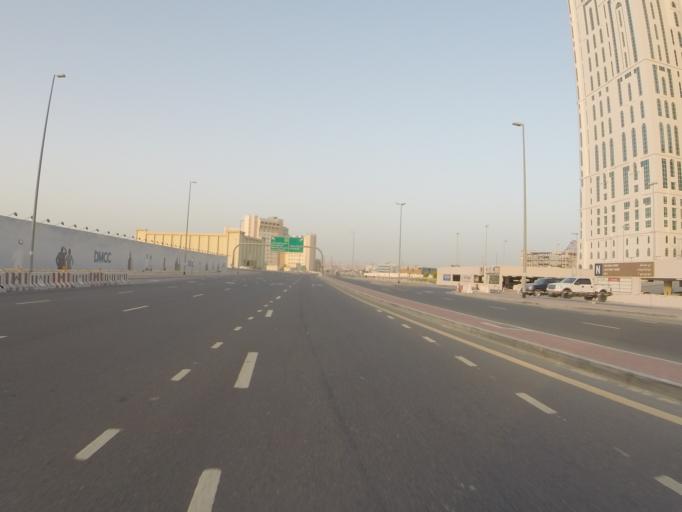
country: AE
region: Dubai
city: Dubai
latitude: 25.0627
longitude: 55.1392
